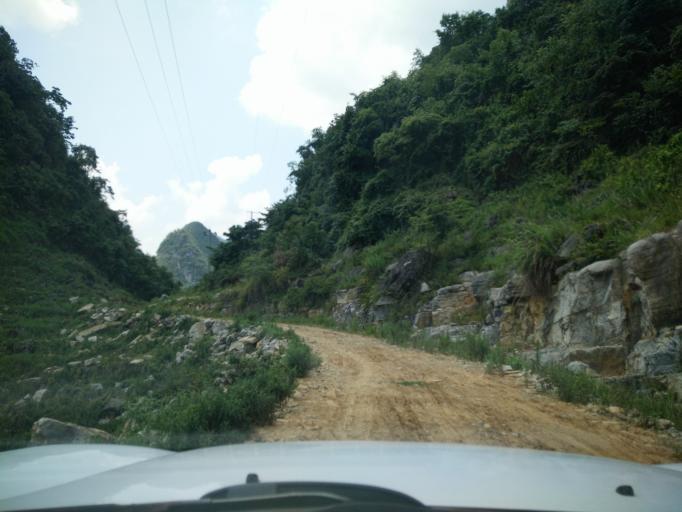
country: CN
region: Guangxi Zhuangzu Zizhiqu
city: Xinzhou
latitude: 25.0058
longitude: 105.7033
